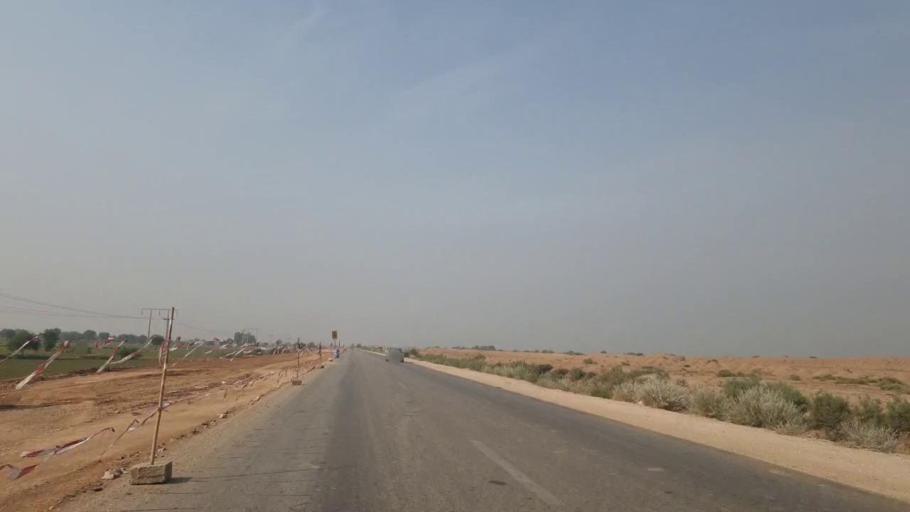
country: PK
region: Sindh
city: Sann
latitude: 26.1356
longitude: 68.0440
